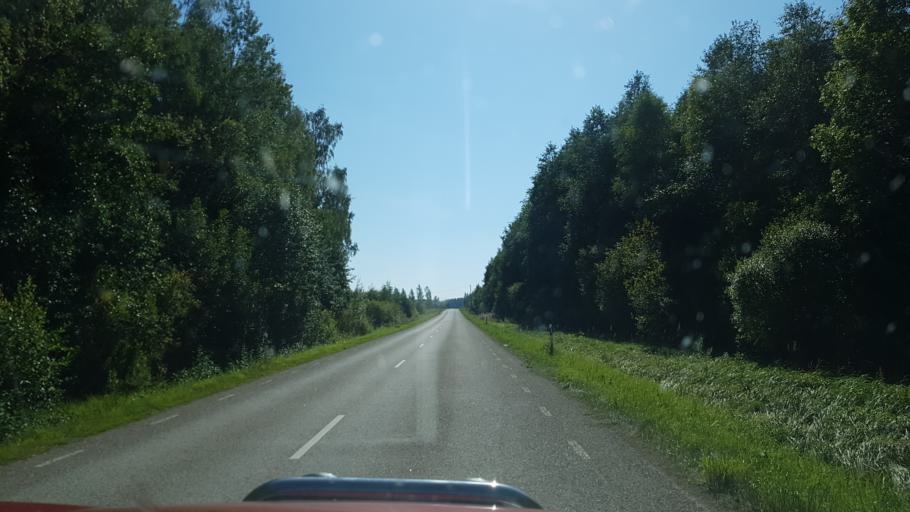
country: EE
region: Polvamaa
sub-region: Polva linn
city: Polva
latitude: 58.2311
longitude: 27.2221
